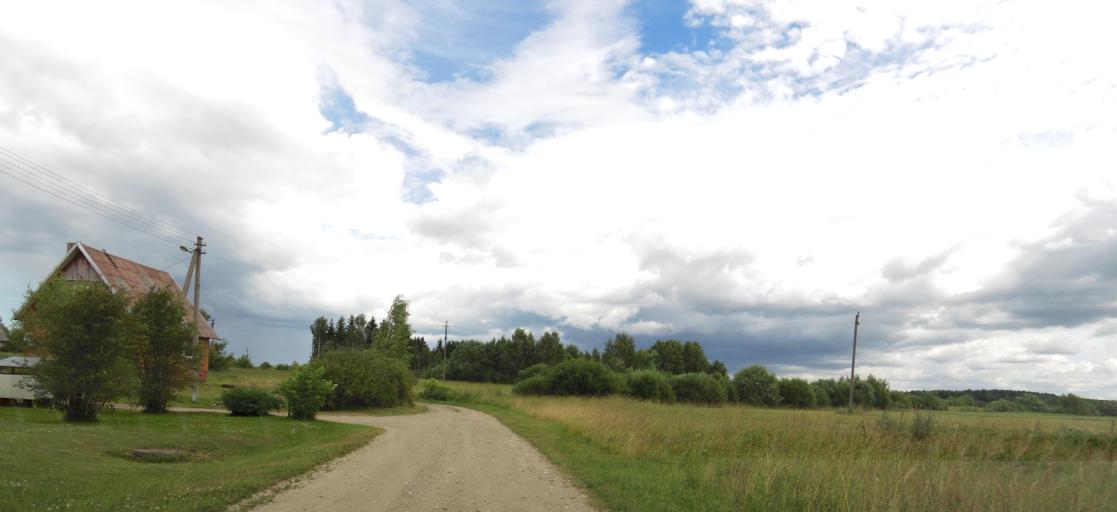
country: LT
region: Panevezys
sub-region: Birzai
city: Birzai
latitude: 56.3938
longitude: 24.7775
